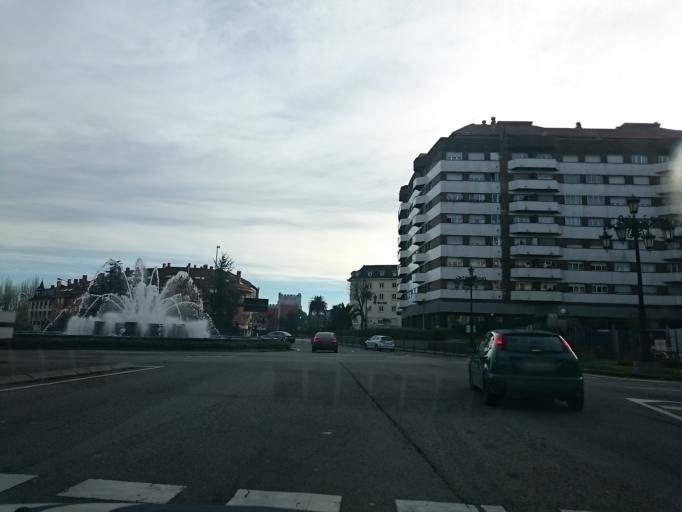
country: ES
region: Asturias
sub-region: Province of Asturias
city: Oviedo
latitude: 43.3584
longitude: -5.8382
